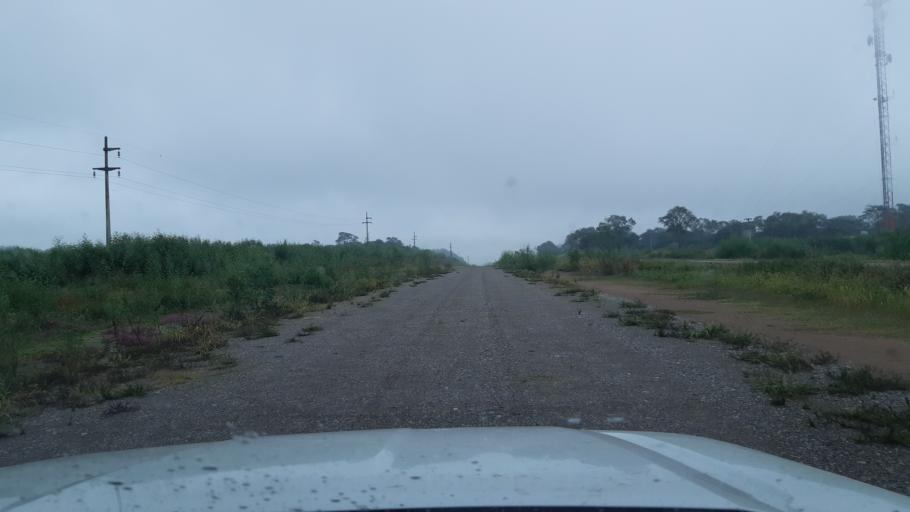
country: AR
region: Jujuy
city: La Mendieta
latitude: -24.3757
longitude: -65.0105
